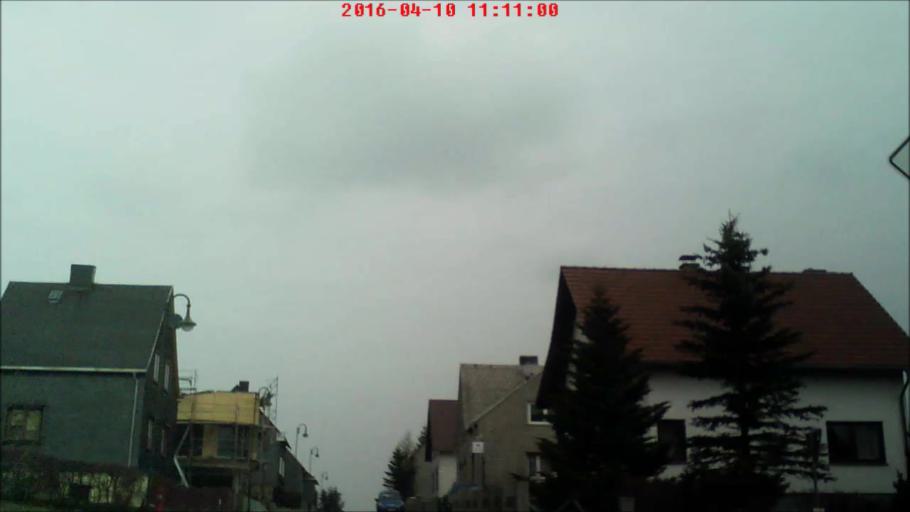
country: DE
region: Thuringia
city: Frauenwald
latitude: 50.5764
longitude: 10.8584
